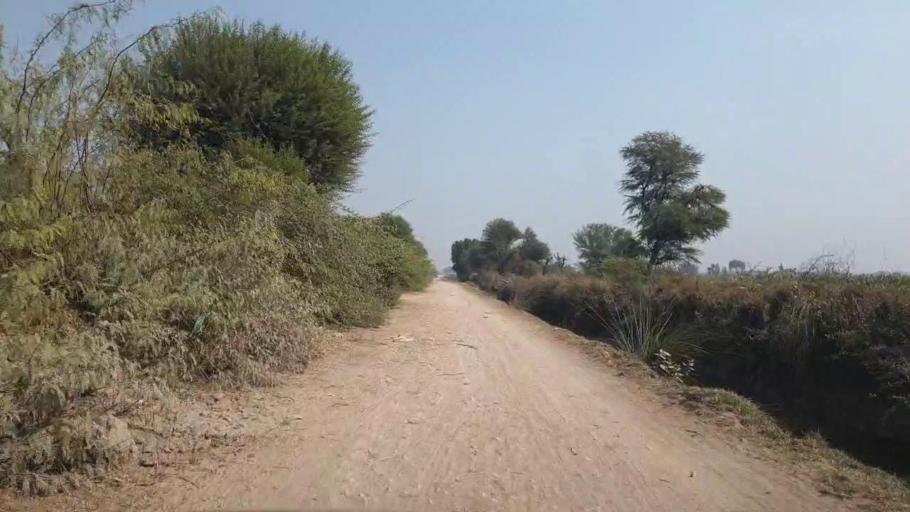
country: PK
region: Sindh
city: Bhit Shah
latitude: 25.7723
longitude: 68.4871
